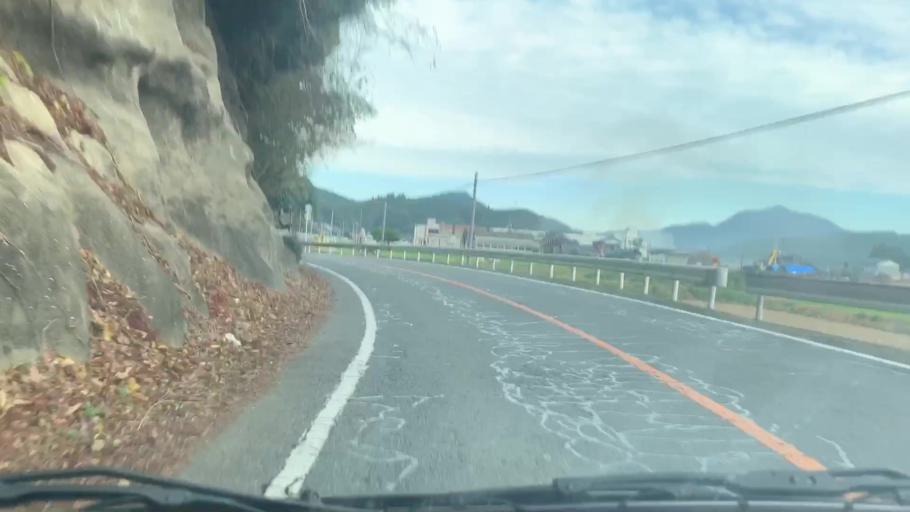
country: JP
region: Saga Prefecture
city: Takeocho-takeo
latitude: 33.2245
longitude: 129.9644
